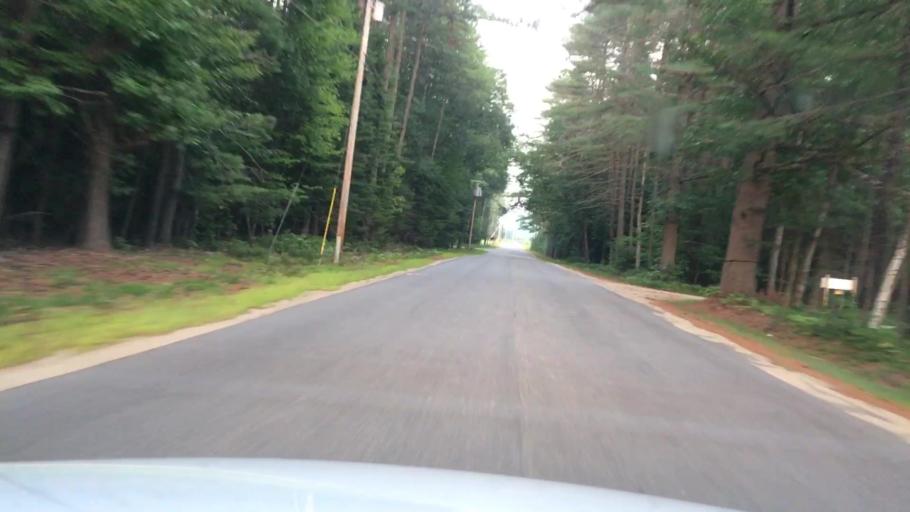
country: US
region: Maine
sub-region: Oxford County
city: Bethel
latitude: 44.4210
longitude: -70.8125
